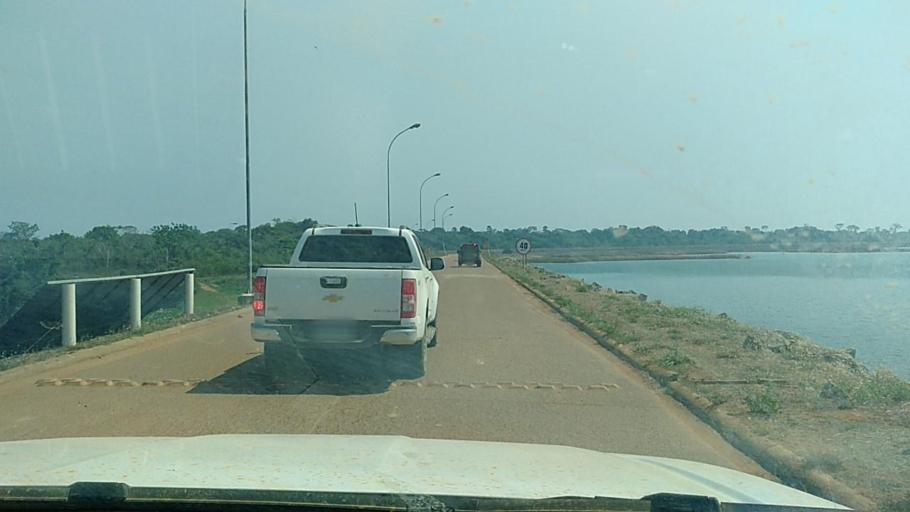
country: BR
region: Rondonia
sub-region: Porto Velho
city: Porto Velho
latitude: -8.7505
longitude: -63.4538
